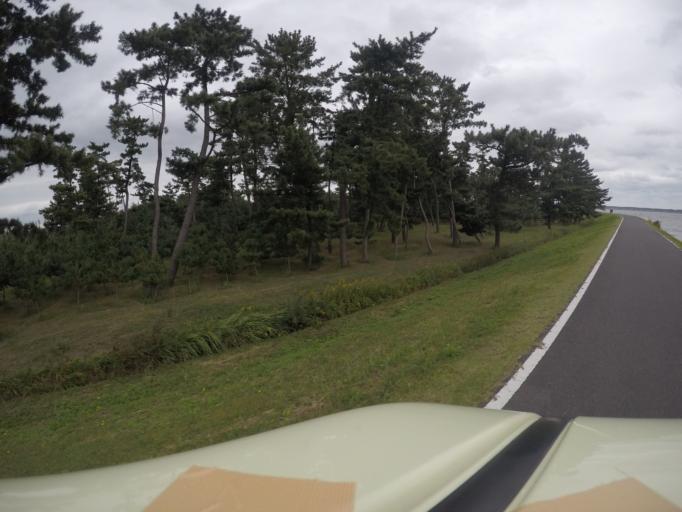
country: JP
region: Chiba
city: Katori-shi
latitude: 35.9738
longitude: 140.4483
